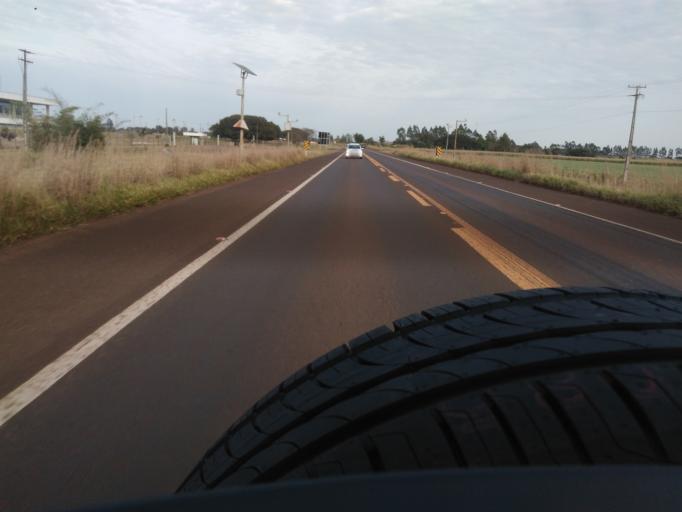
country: BR
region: Mato Grosso do Sul
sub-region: Ponta Pora
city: Ponta Pora
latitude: -22.6185
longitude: -55.6083
